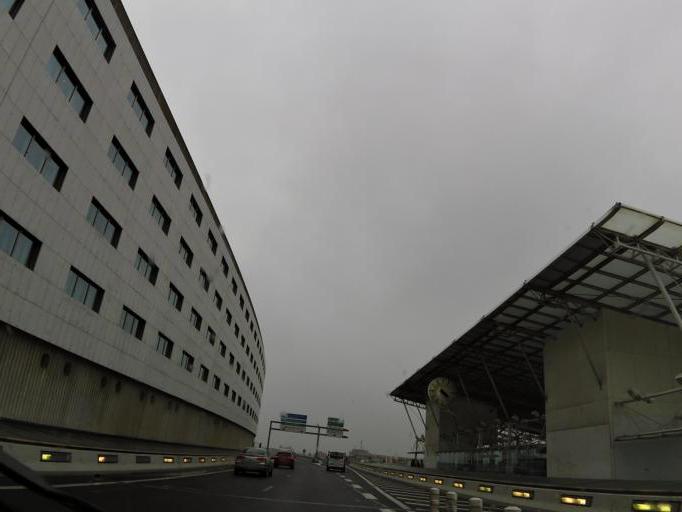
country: FR
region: Ile-de-France
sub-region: Departement de Seine-et-Marne
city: Mitry-Mory
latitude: 49.0042
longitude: 2.5715
